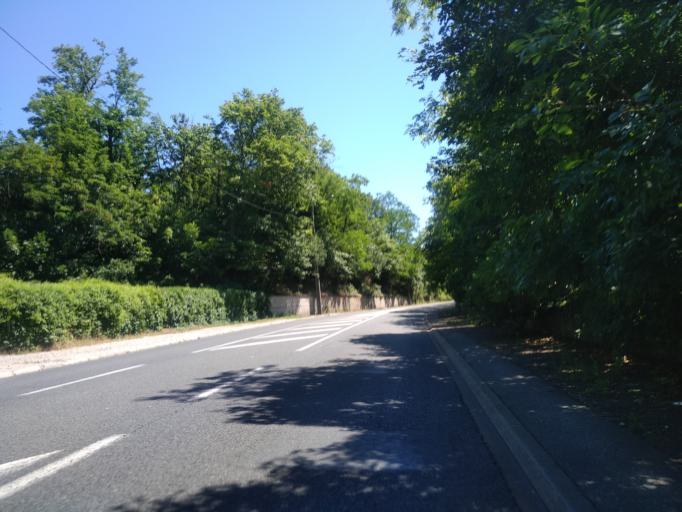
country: FR
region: Rhone-Alpes
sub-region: Departement du Rhone
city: Sathonay-Camp
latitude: 45.8253
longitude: 4.8606
